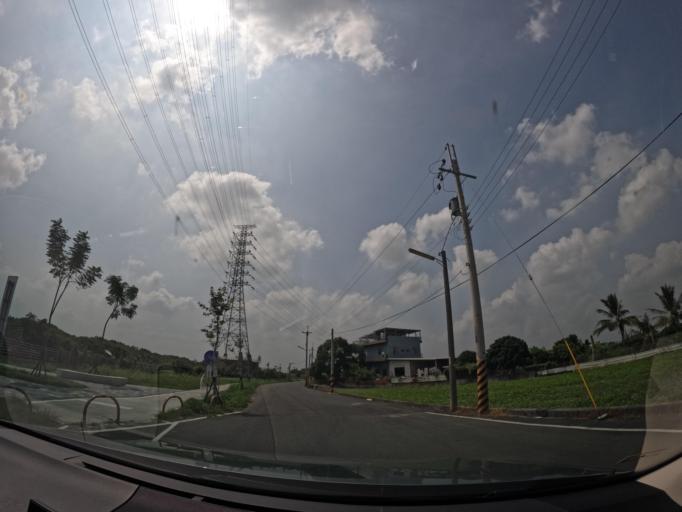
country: TW
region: Taiwan
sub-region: Yunlin
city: Douliu
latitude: 23.6697
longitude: 120.4003
